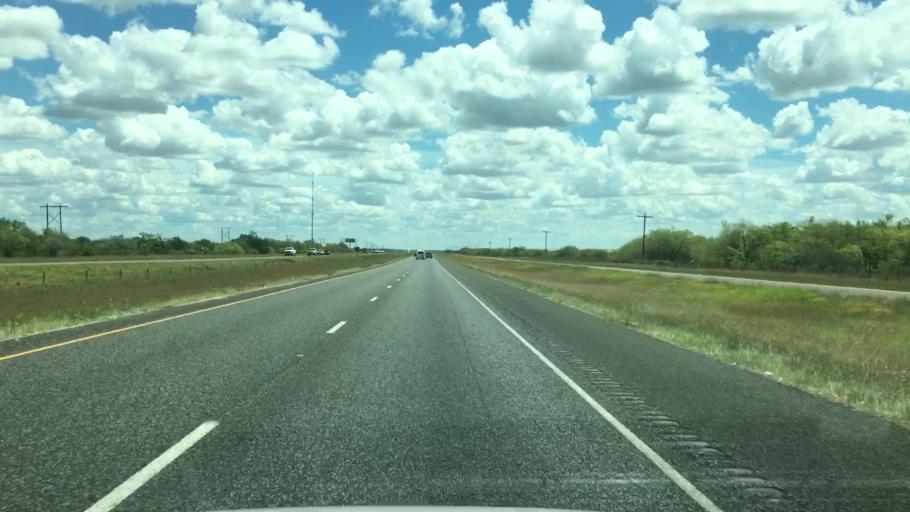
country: US
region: Texas
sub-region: Atascosa County
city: Pleasanton
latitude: 28.8080
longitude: -98.3494
